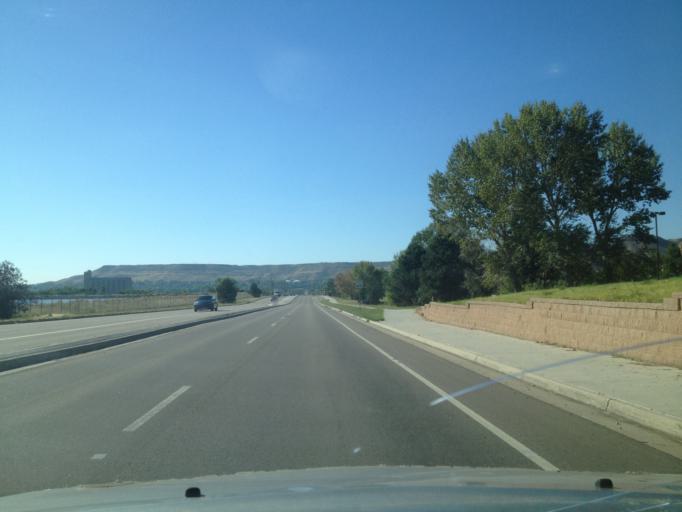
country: US
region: Colorado
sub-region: Jefferson County
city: Applewood
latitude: 39.7826
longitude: -105.1749
